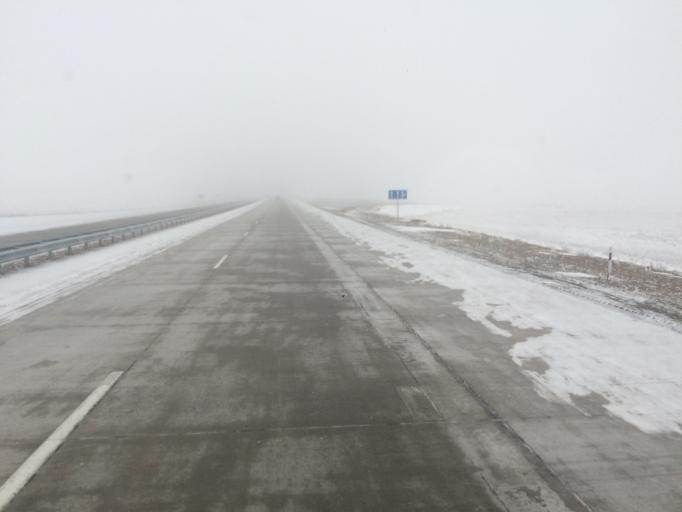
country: KZ
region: Zhambyl
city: Georgiyevka
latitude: 43.4141
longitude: 75.0355
